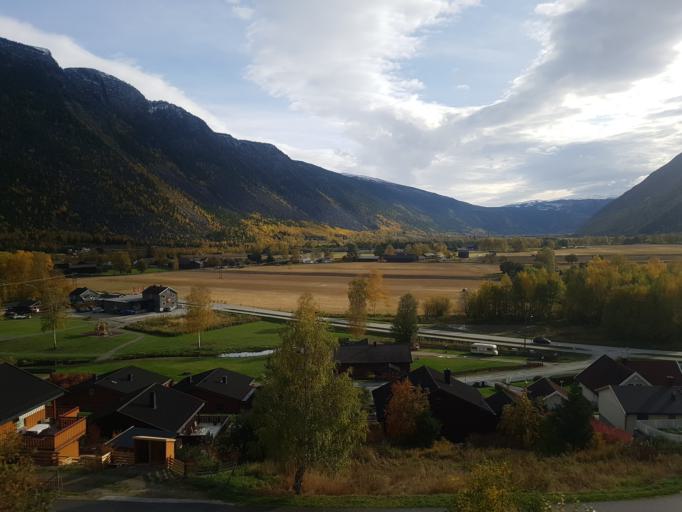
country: NO
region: Oppland
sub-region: Sel
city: Otta
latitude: 61.8475
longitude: 9.4169
